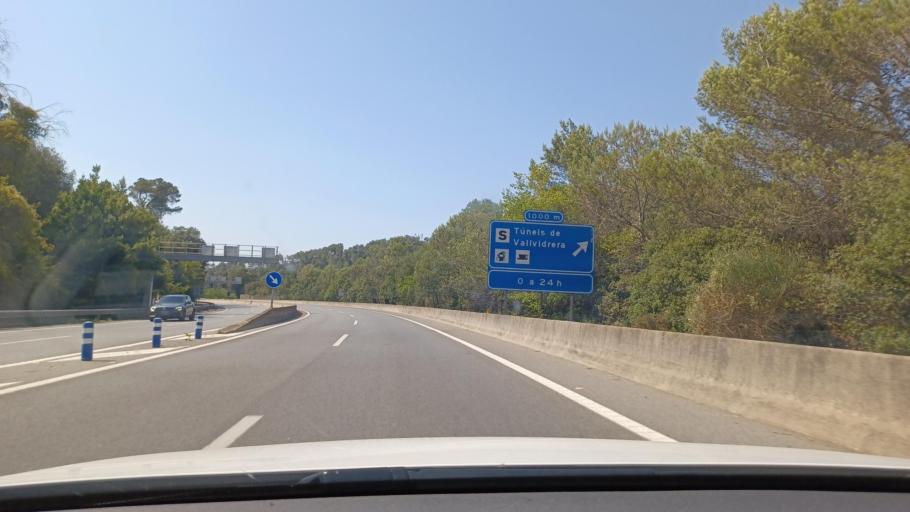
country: ES
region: Catalonia
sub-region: Provincia de Barcelona
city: Sant Cugat del Valles
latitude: 41.4258
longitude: 2.0919
